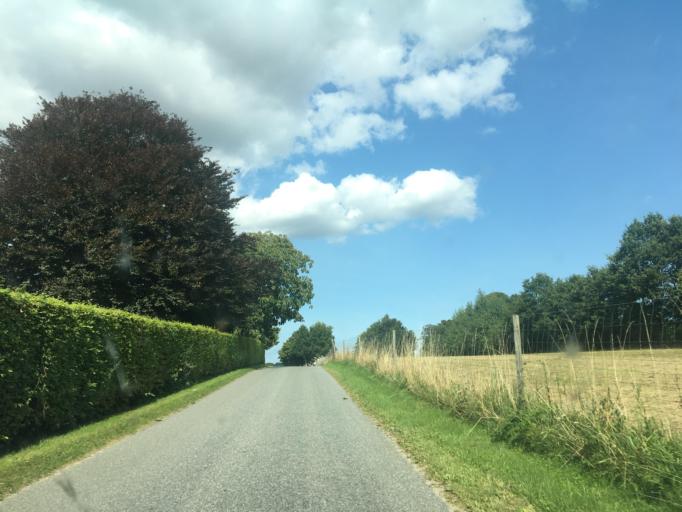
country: DK
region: South Denmark
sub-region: Middelfart Kommune
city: Ejby
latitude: 55.3964
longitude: 9.9230
